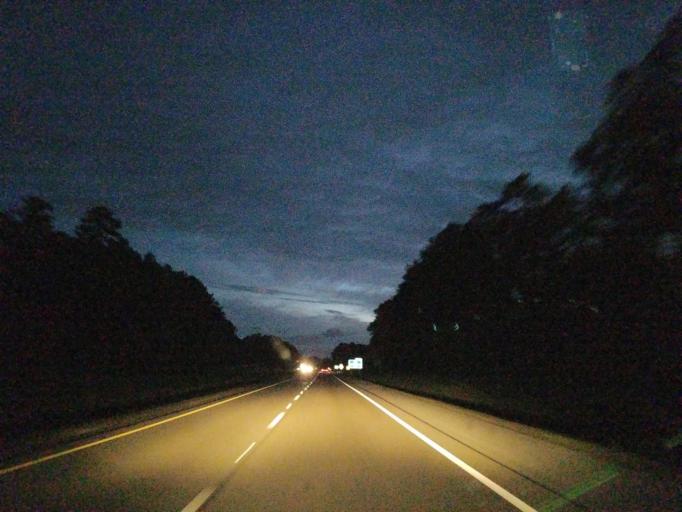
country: US
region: Mississippi
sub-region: Jones County
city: Laurel
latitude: 31.7267
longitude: -89.1013
